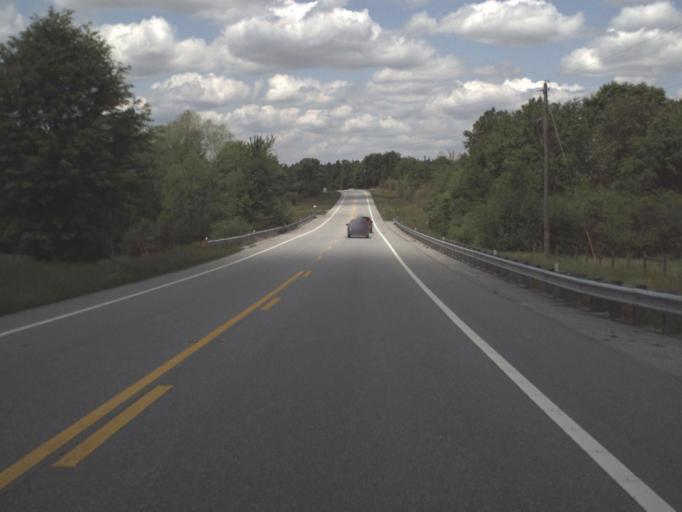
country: US
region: Florida
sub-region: Escambia County
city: Molino
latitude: 30.8089
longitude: -87.4253
